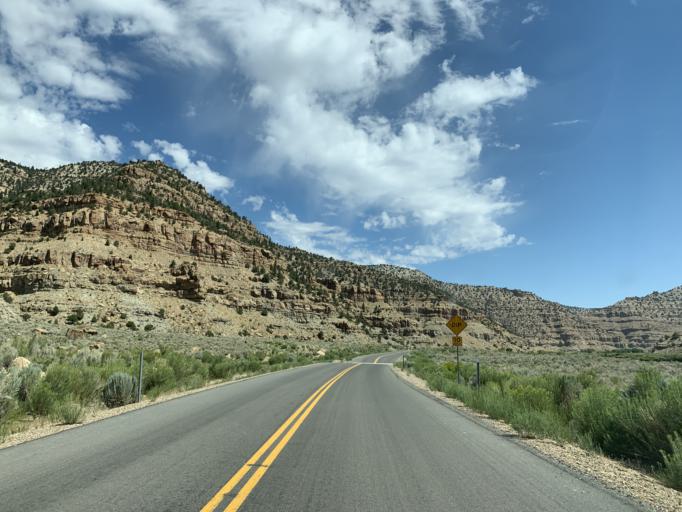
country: US
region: Utah
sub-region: Carbon County
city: East Carbon City
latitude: 39.7907
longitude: -110.3932
